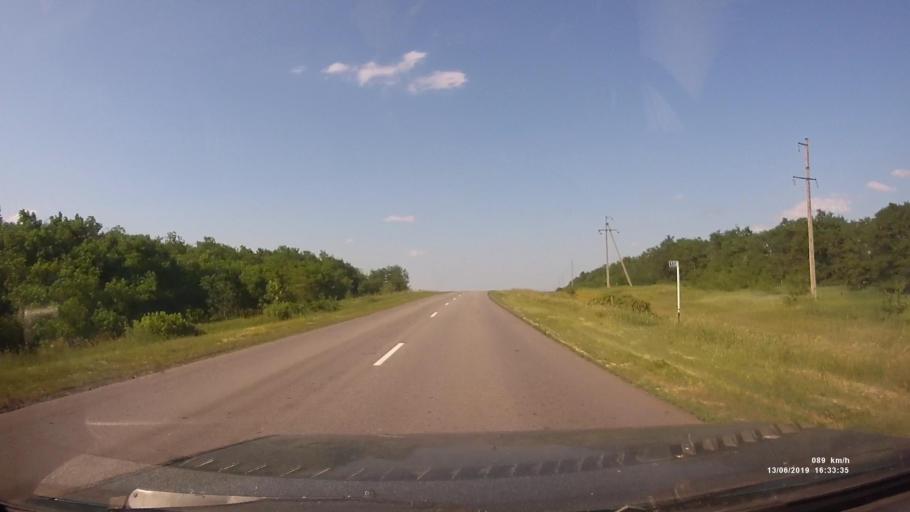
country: RU
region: Rostov
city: Kazanskaya
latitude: 49.8625
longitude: 41.2817
